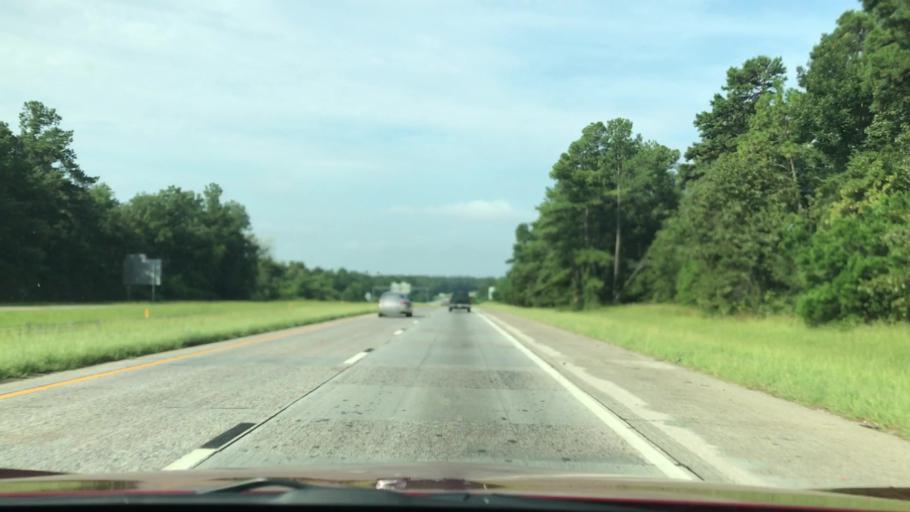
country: US
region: South Carolina
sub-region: Aiken County
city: Belvedere
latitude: 33.5579
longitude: -81.9452
